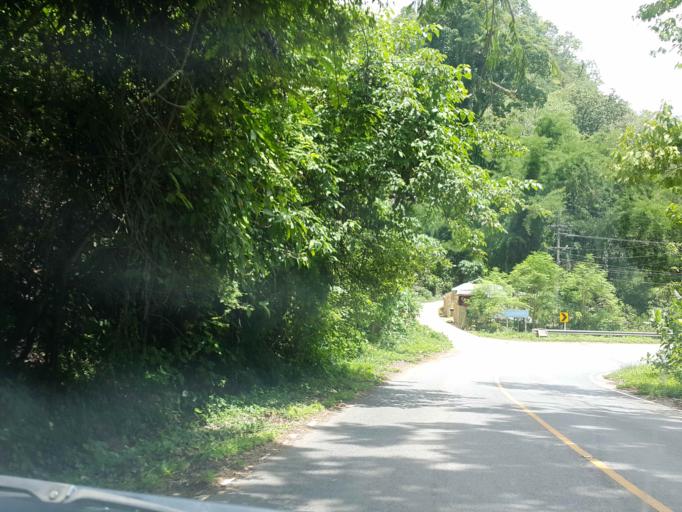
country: TH
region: Chiang Mai
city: Samoeng
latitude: 18.8002
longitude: 98.7956
